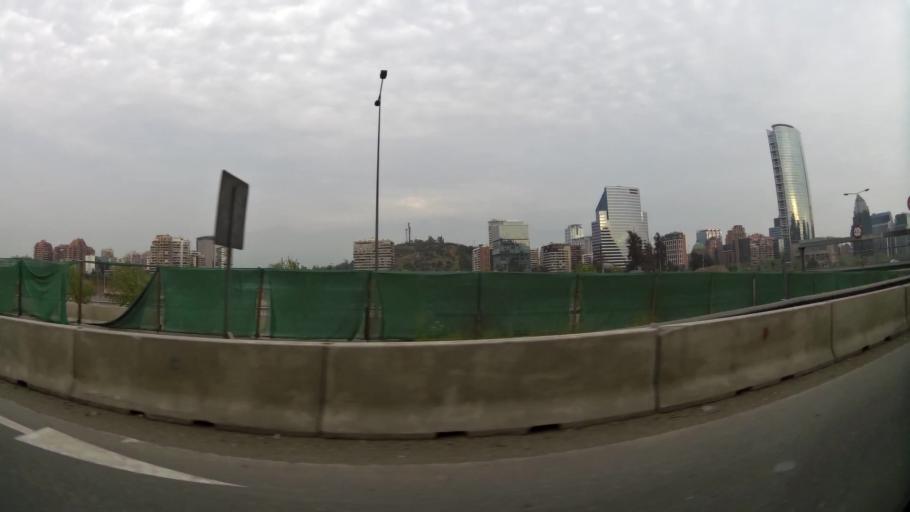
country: CL
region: Santiago Metropolitan
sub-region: Provincia de Santiago
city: Villa Presidente Frei, Nunoa, Santiago, Chile
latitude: -33.4078
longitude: -70.6057
